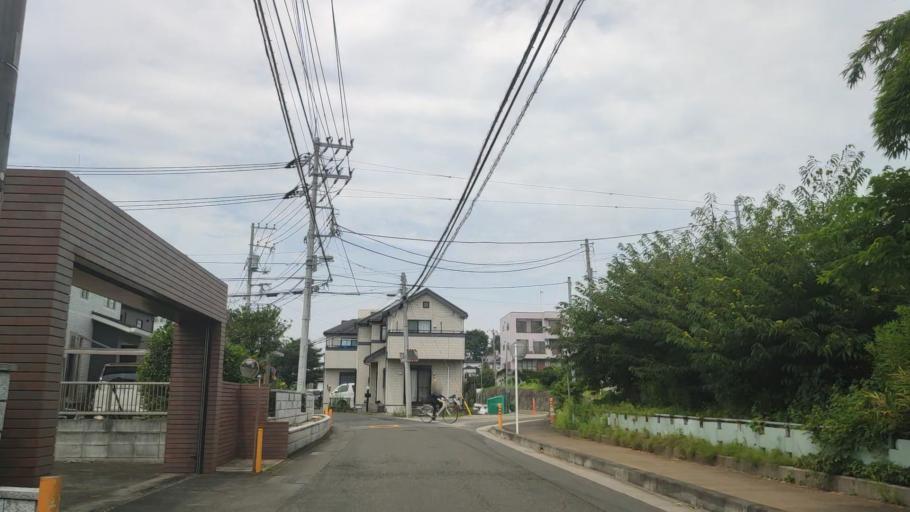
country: JP
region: Kanagawa
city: Atsugi
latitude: 35.4231
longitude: 139.3966
